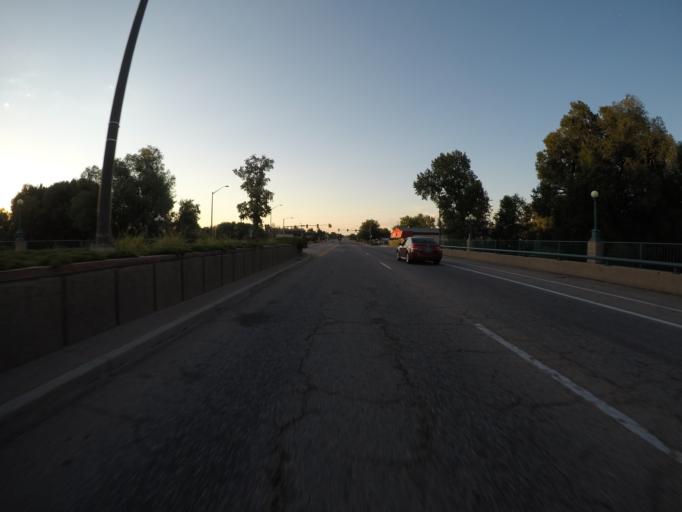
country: US
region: Colorado
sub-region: Larimer County
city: Fort Collins
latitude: 40.5953
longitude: -105.0767
